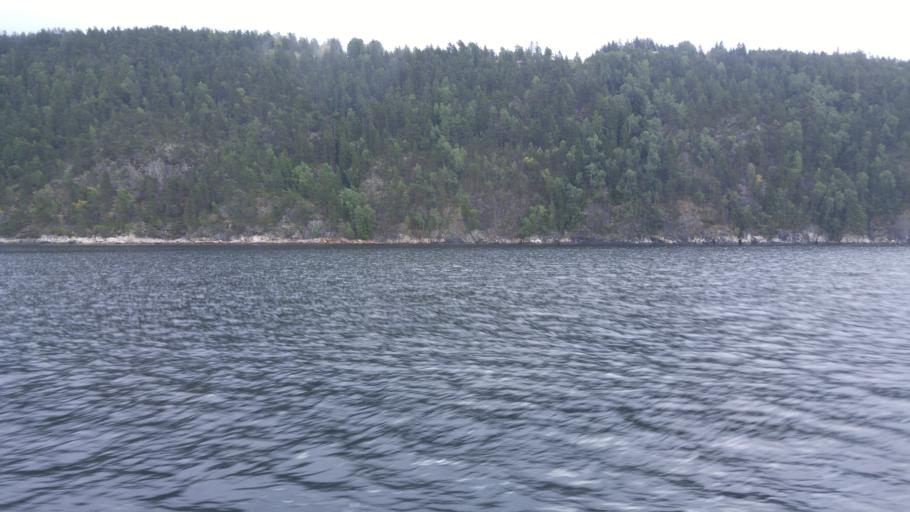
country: NO
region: Akershus
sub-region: Nesodden
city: Fagerstrand
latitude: 59.8100
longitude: 10.6083
